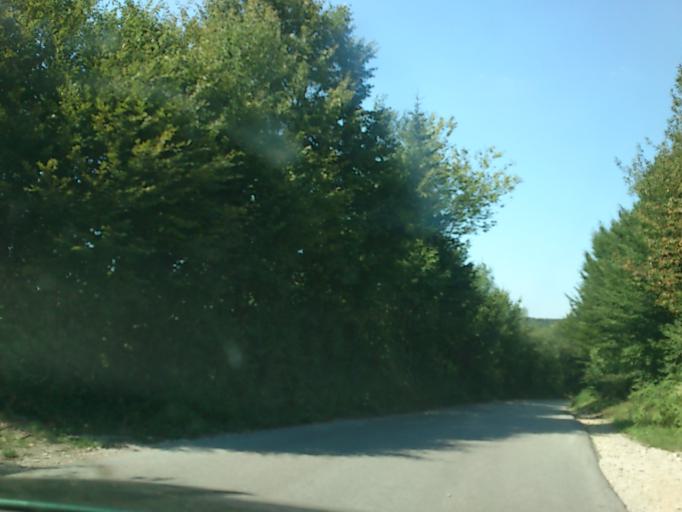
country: HR
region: Licko-Senjska
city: Otocac
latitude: 44.8458
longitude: 15.1463
